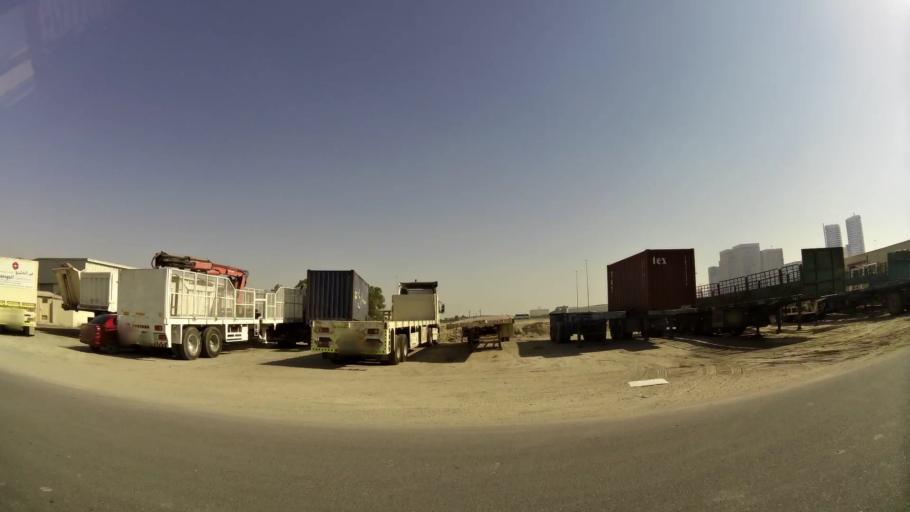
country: AE
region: Dubai
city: Dubai
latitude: 24.9876
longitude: 55.1015
